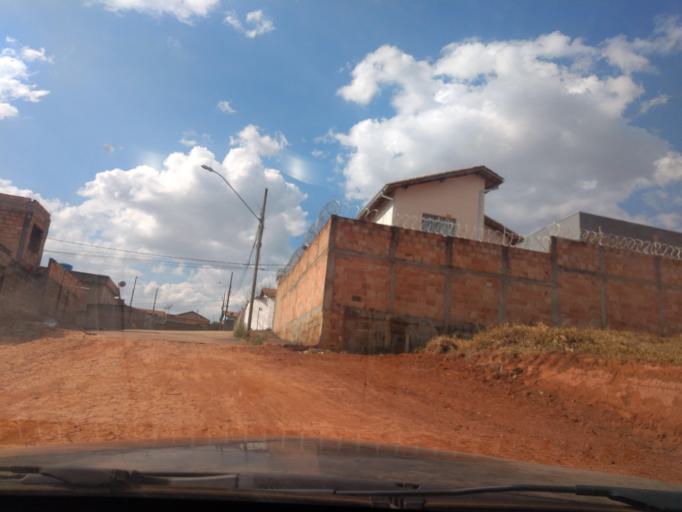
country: BR
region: Minas Gerais
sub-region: Tres Coracoes
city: Tres Coracoes
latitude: -21.6854
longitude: -45.2368
